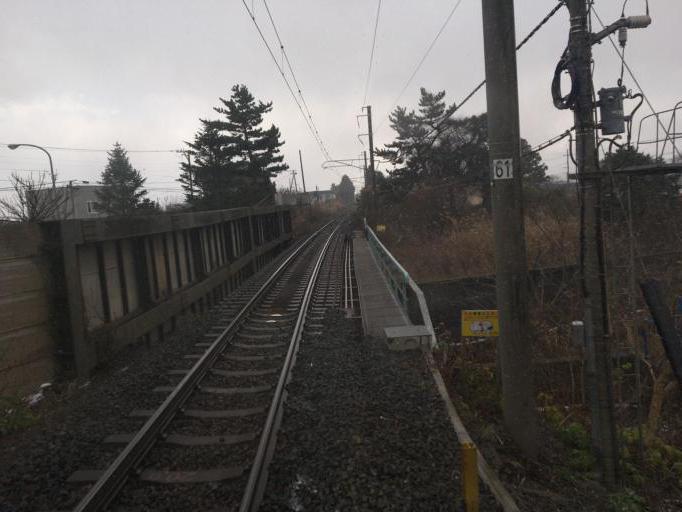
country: JP
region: Aomori
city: Aomori Shi
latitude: 40.9827
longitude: 140.6538
